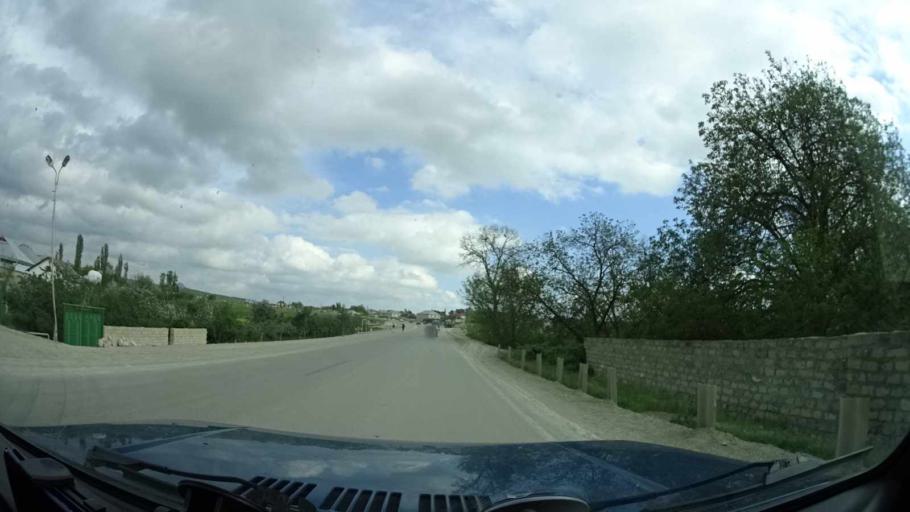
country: AZ
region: Samaxi
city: Shamakhi
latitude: 40.5938
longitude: 48.7027
